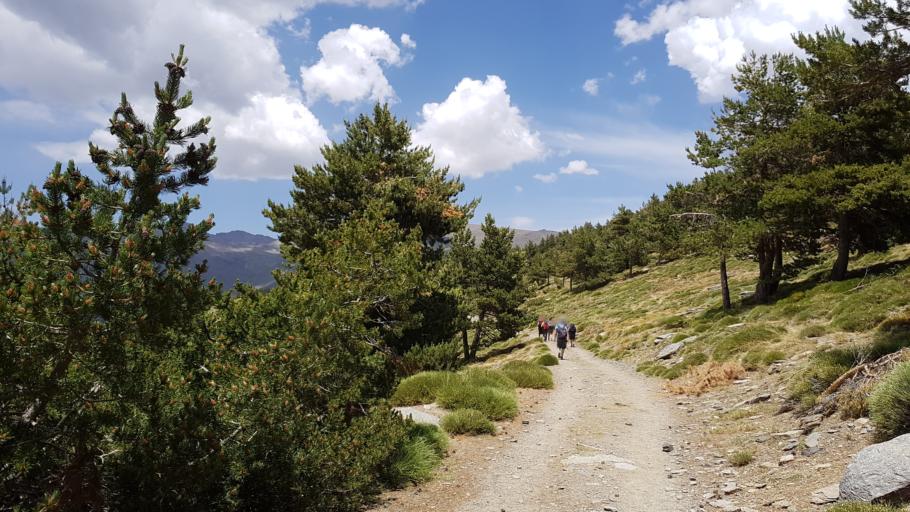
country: ES
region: Andalusia
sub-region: Provincia de Granada
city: Capileira
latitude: 36.9852
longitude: -3.3289
